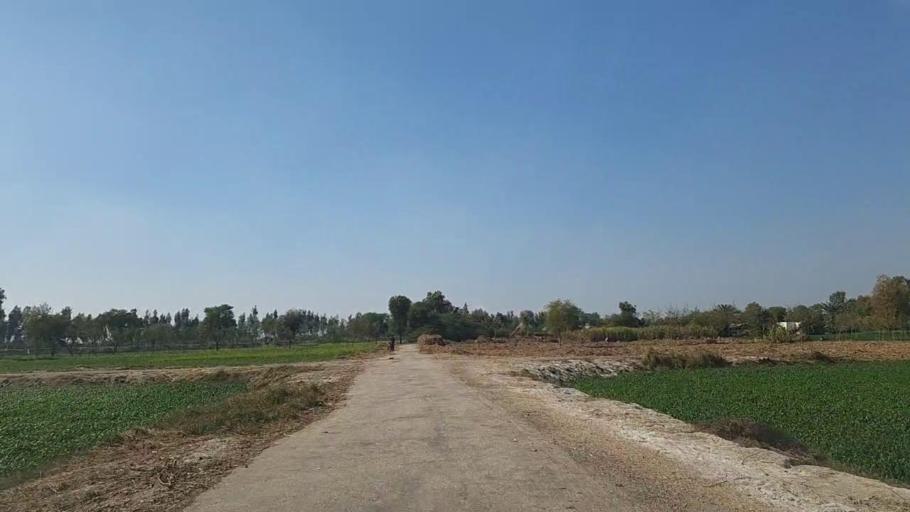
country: PK
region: Sindh
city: Nawabshah
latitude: 26.3470
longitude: 68.3834
